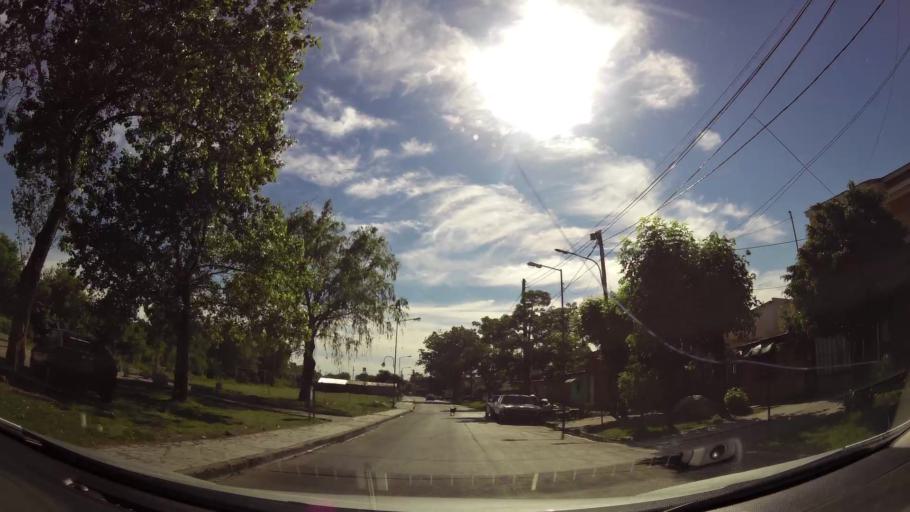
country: AR
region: Buenos Aires
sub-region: Partido de Tigre
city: Tigre
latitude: -34.4751
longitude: -58.5804
